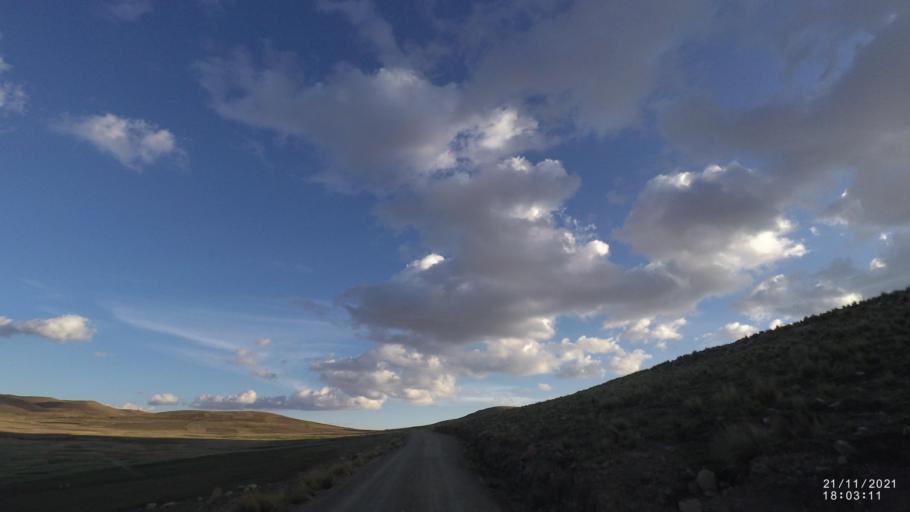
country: BO
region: Cochabamba
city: Cochabamba
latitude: -17.2587
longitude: -66.2250
